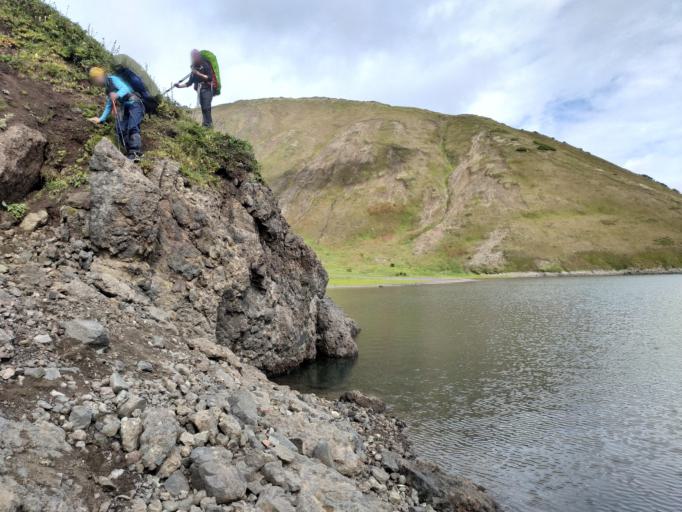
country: RU
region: Kamtsjatka
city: Yelizovo
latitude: 53.8649
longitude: 158.0229
